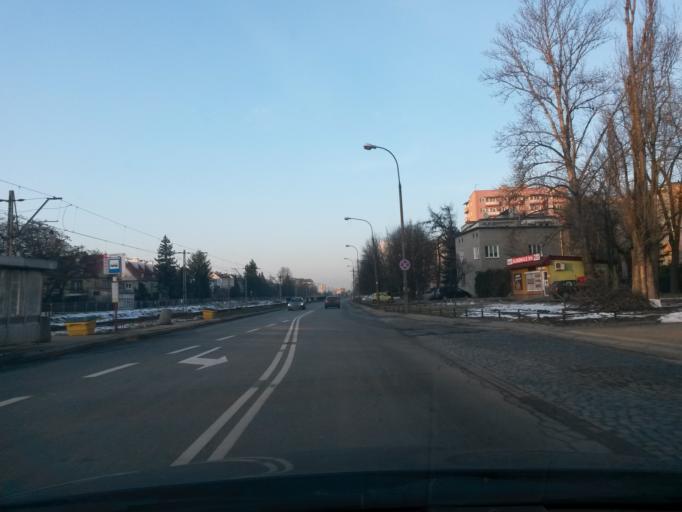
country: PL
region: Masovian Voivodeship
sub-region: Warszawa
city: Mokotow
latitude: 52.1895
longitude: 21.0022
